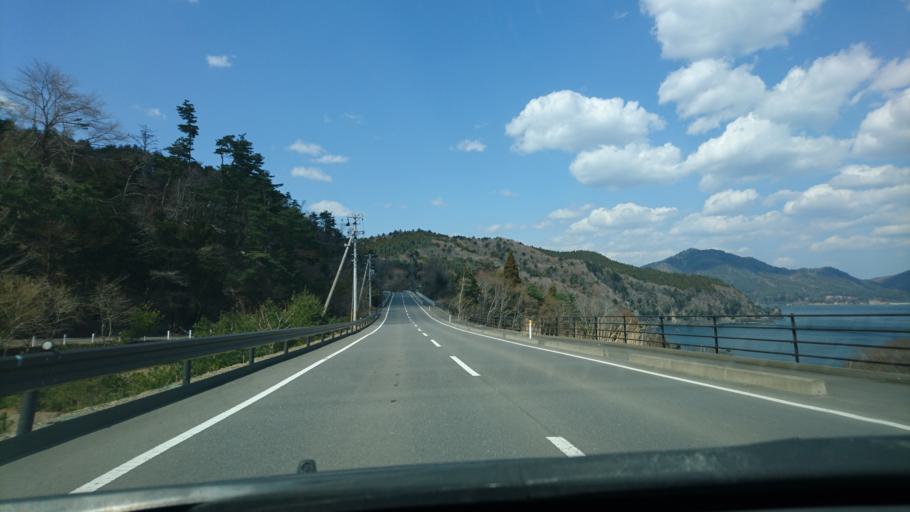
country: JP
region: Miyagi
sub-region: Oshika Gun
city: Onagawa Cho
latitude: 38.4836
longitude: 141.4927
